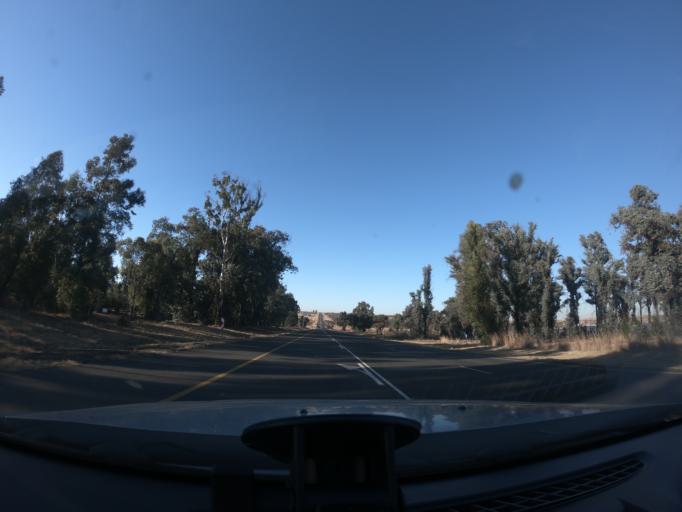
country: ZA
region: Mpumalanga
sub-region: Gert Sibande District Municipality
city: Ermelo
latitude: -26.4614
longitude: 29.9525
